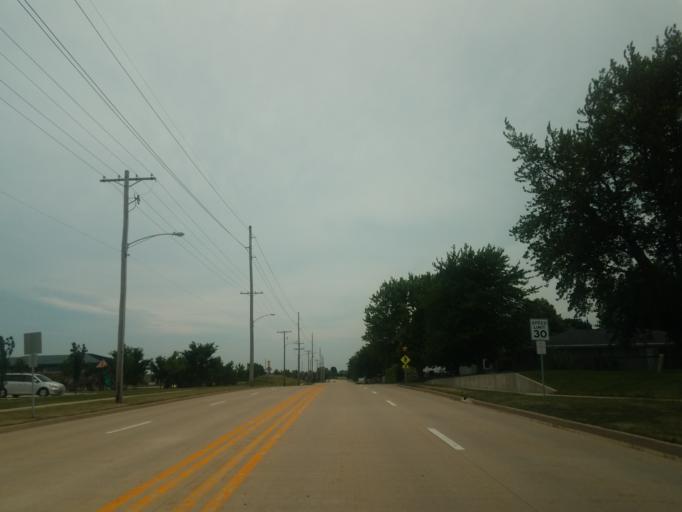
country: US
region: Illinois
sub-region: McLean County
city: Normal
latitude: 40.5220
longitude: -88.9437
